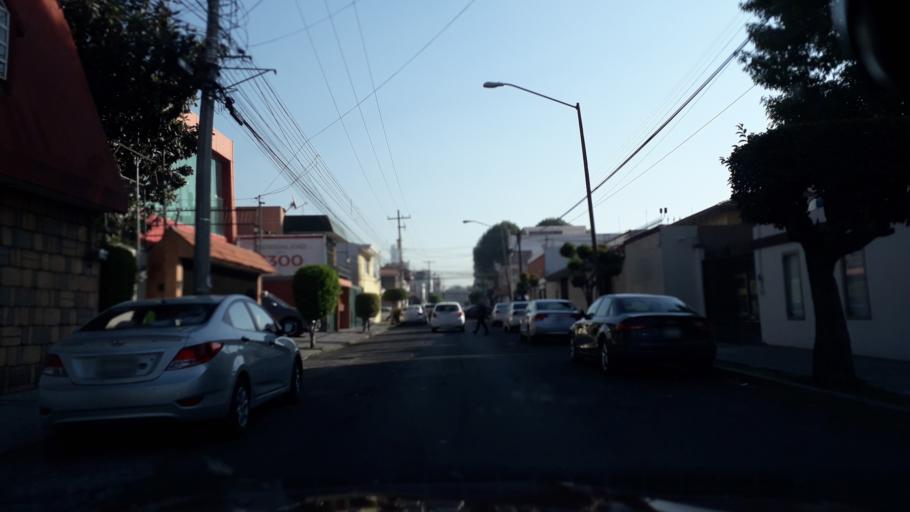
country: MX
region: Puebla
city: Puebla
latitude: 19.0412
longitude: -98.2277
